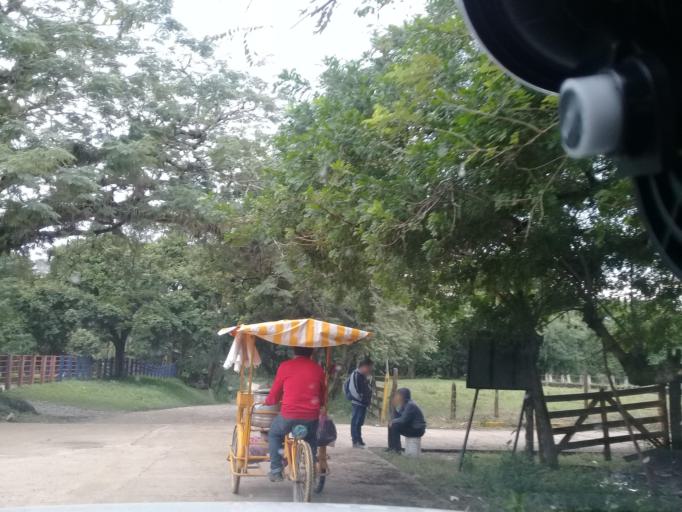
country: MX
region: Hidalgo
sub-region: Huejutla de Reyes
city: Chalahuiyapa
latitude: 21.1618
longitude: -98.3633
